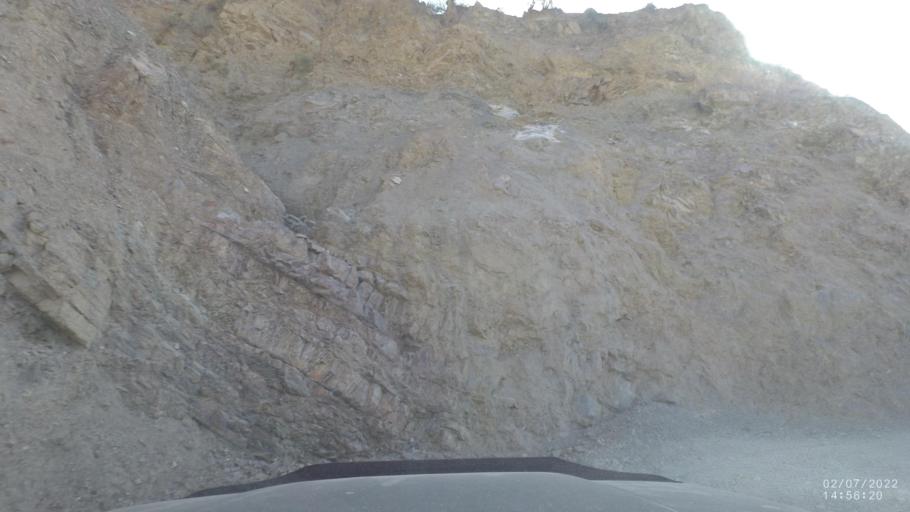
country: BO
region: Cochabamba
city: Irpa Irpa
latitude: -17.8560
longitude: -66.4355
